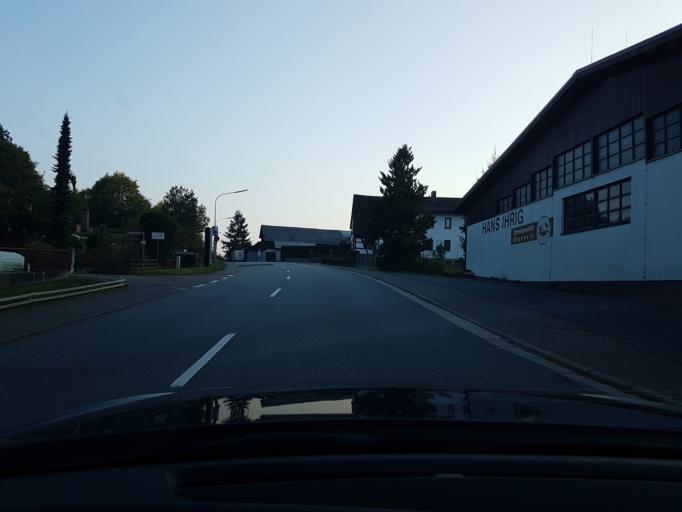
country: DE
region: Hesse
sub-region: Regierungsbezirk Darmstadt
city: Beerfelden
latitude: 49.5258
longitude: 8.9656
